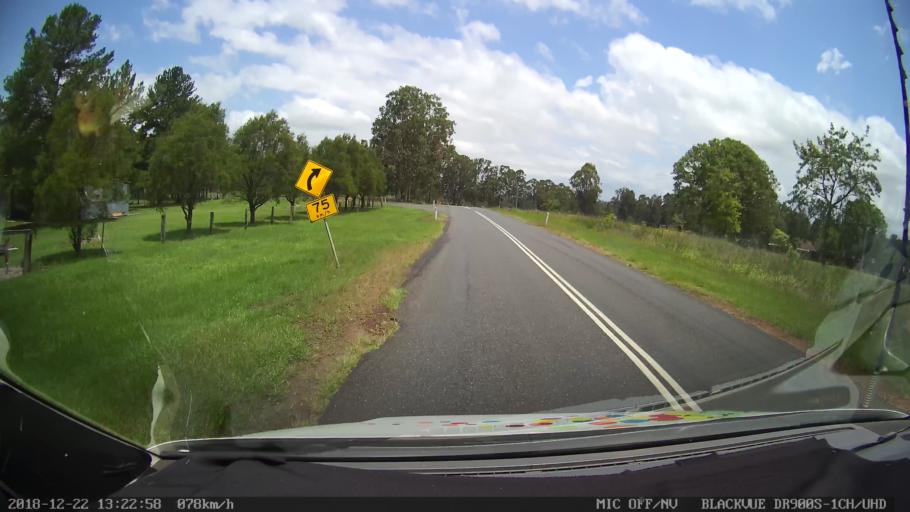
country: AU
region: New South Wales
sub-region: Clarence Valley
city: Coutts Crossing
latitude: -29.7930
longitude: 152.9097
